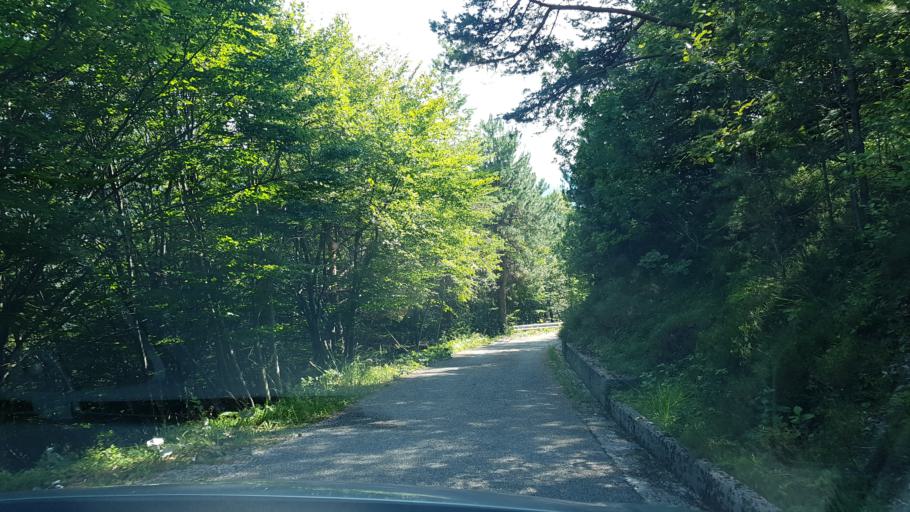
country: IT
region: Friuli Venezia Giulia
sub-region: Provincia di Udine
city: Moggio Udinese
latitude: 46.4459
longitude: 13.2154
